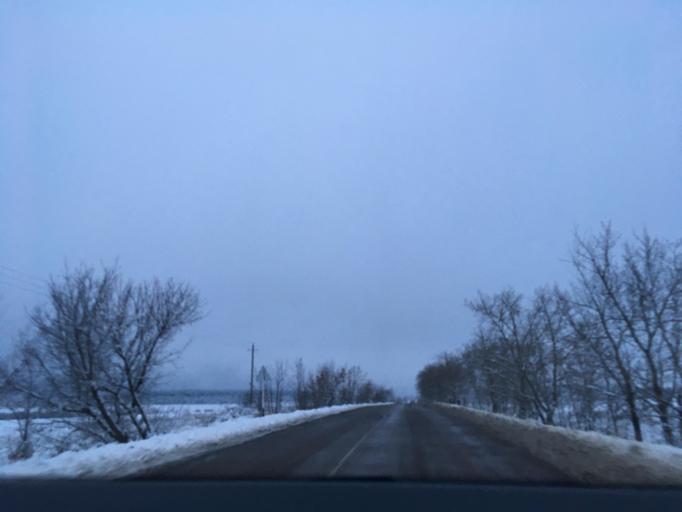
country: RU
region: Voronezj
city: Verkhniy Mamon
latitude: 50.0600
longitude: 40.2625
